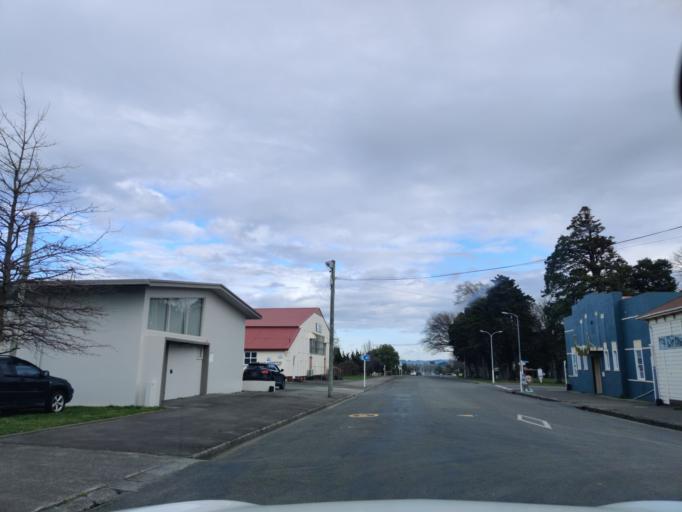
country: NZ
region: Manawatu-Wanganui
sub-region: Palmerston North City
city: Palmerston North
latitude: -40.3383
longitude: 175.8693
